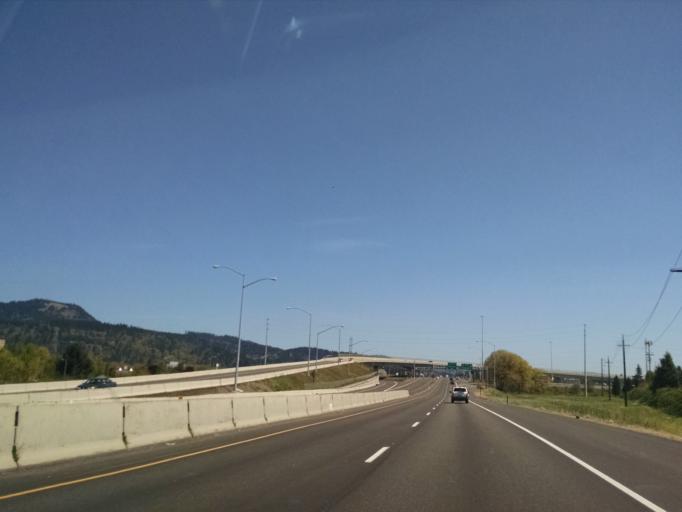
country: US
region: Oregon
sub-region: Lane County
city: Eugene
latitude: 44.0841
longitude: -123.0544
